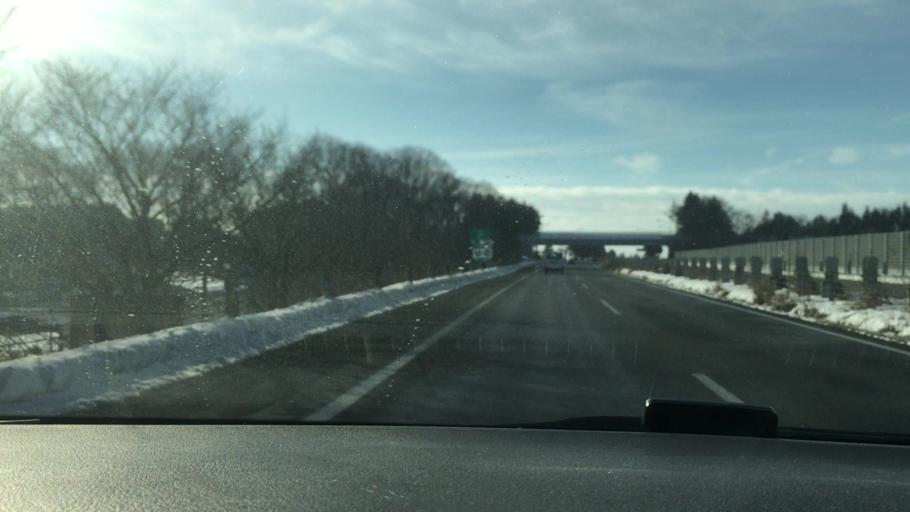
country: JP
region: Iwate
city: Hanamaki
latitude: 39.3732
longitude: 141.0930
